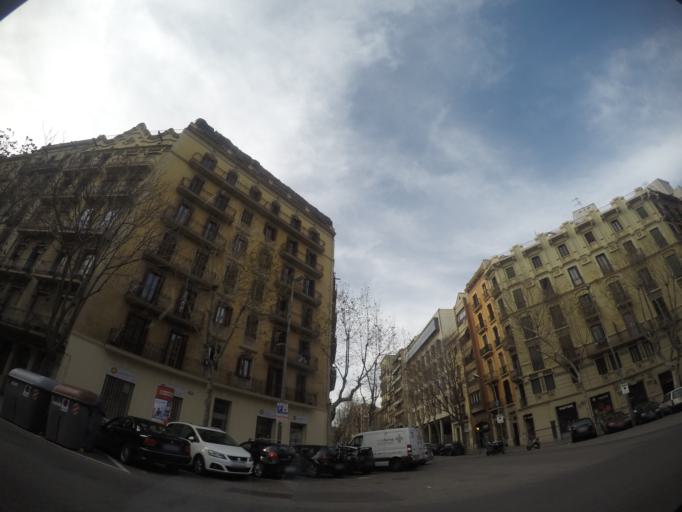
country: ES
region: Catalonia
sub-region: Provincia de Barcelona
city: Eixample
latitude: 41.3984
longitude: 2.1732
